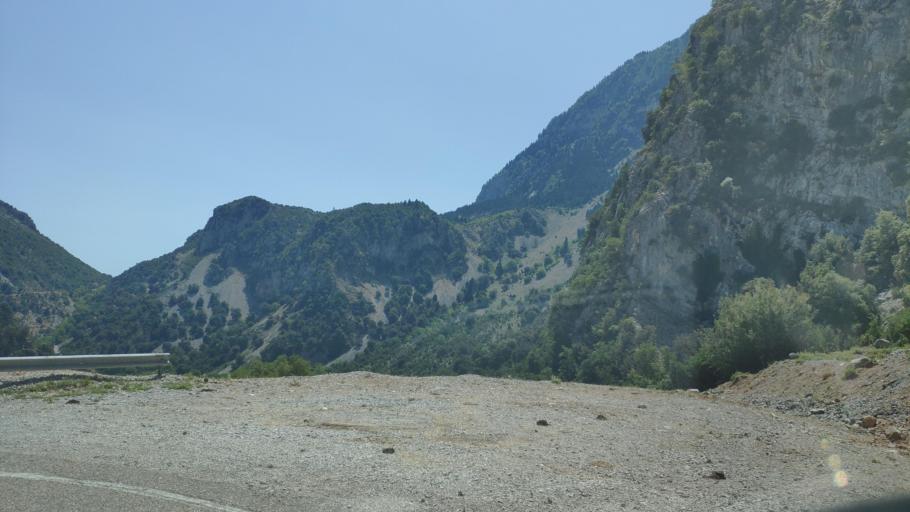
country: GR
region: West Greece
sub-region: Nomos Aitolias kai Akarnanias
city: Krikellos
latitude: 39.0067
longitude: 21.3623
